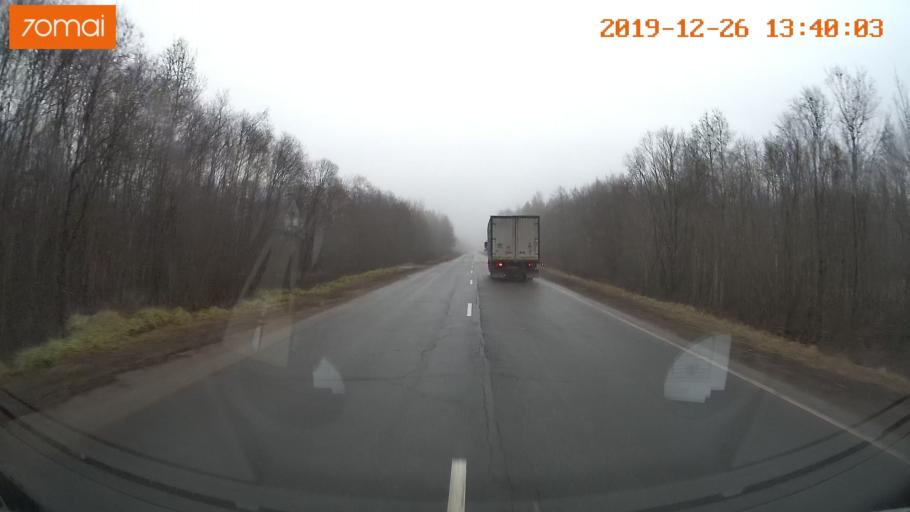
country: RU
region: Vologda
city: Sheksna
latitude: 58.7464
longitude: 38.4223
